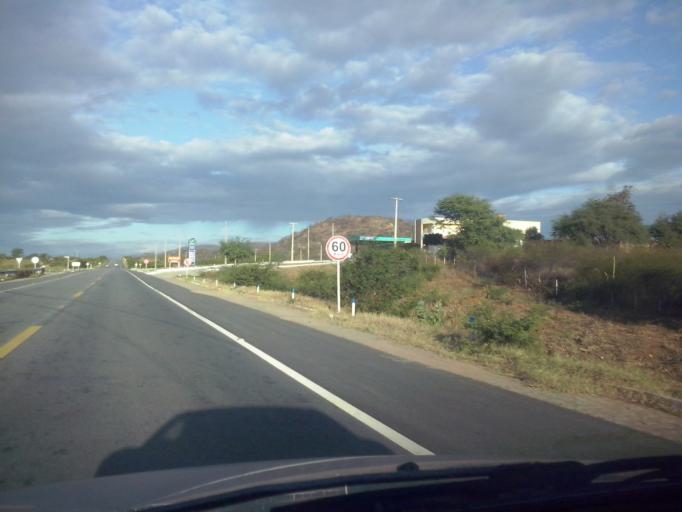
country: BR
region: Paraiba
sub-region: Patos
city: Patos
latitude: -6.9073
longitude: -37.5092
